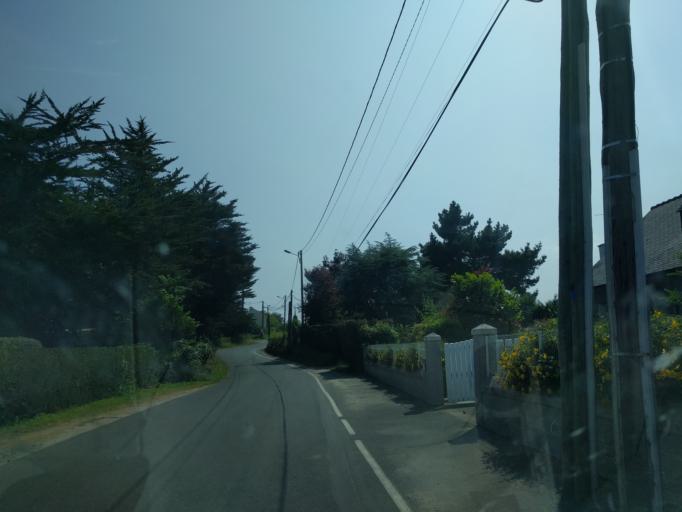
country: FR
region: Brittany
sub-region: Departement des Cotes-d'Armor
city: Plurien
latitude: 48.6421
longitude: -2.4241
